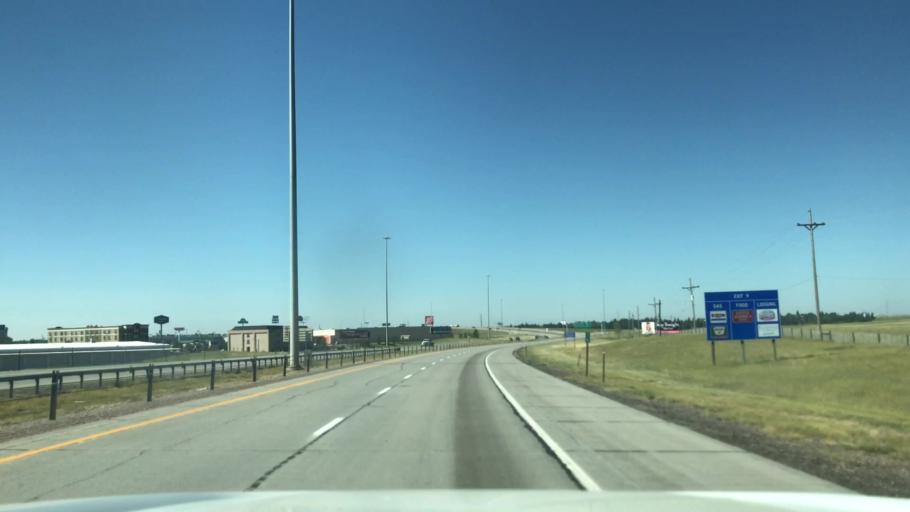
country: US
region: Wyoming
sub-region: Laramie County
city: Cheyenne
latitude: 41.1291
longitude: -104.8437
